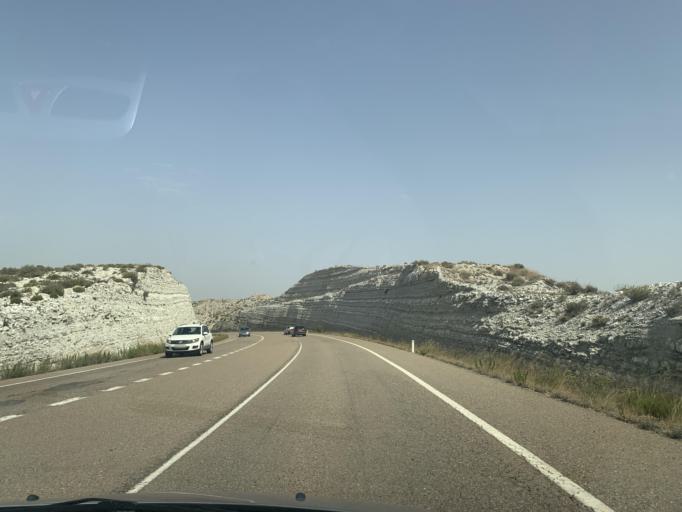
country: ES
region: Aragon
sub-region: Provincia de Zaragoza
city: Fuentes de Ebro
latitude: 41.4509
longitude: -0.7187
